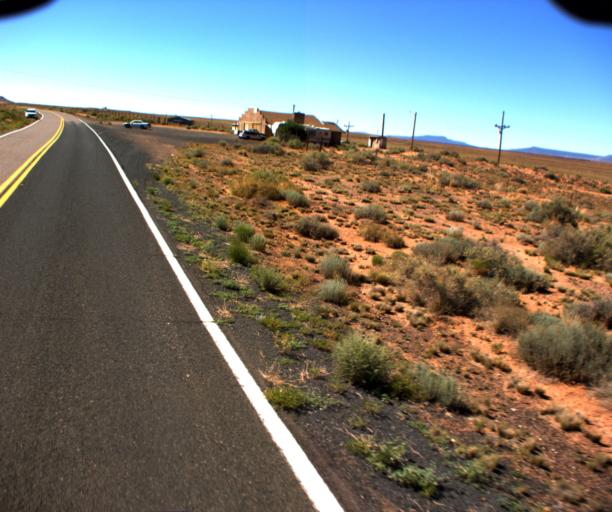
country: US
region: Arizona
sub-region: Coconino County
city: LeChee
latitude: 35.1163
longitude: -110.8725
